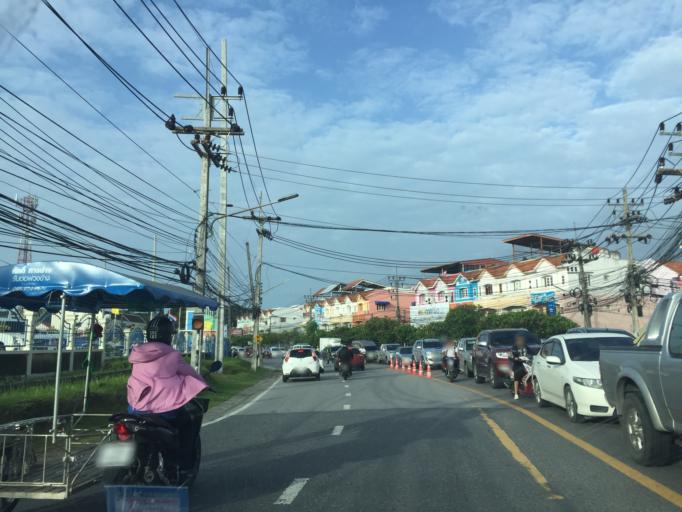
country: TH
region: Phuket
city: Mueang Phuket
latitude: 7.8691
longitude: 98.3744
